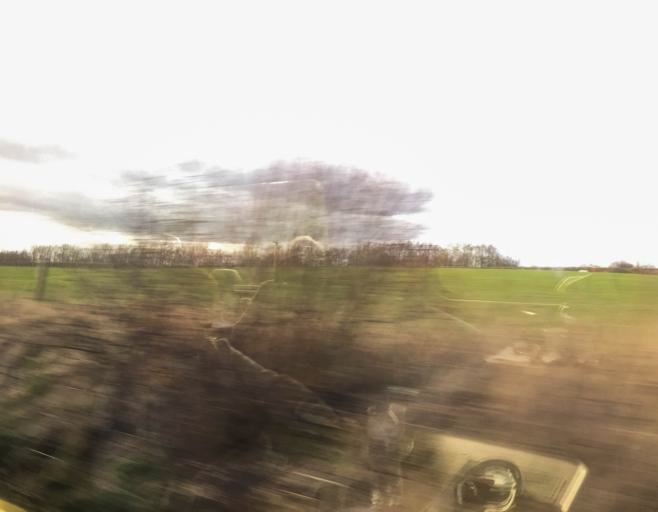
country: GB
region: Scotland
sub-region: Dumfries and Galloway
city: Annan
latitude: 55.0400
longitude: -3.1817
